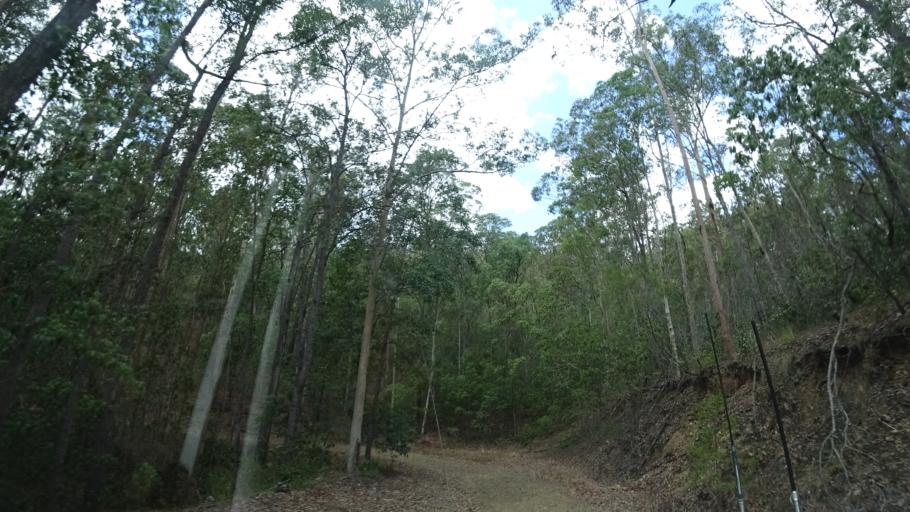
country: AU
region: Queensland
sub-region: Moreton Bay
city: Highvale
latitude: -27.3532
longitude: 152.7240
